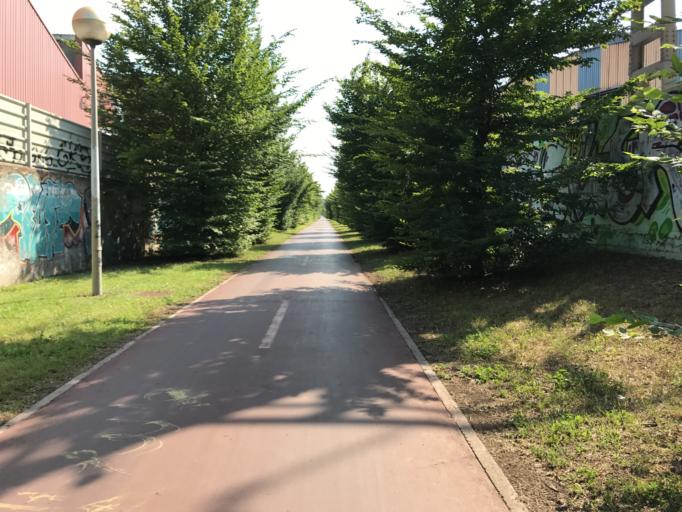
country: ES
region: Basque Country
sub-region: Provincia de Alava
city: Gasteiz / Vitoria
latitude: 42.8671
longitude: -2.6530
